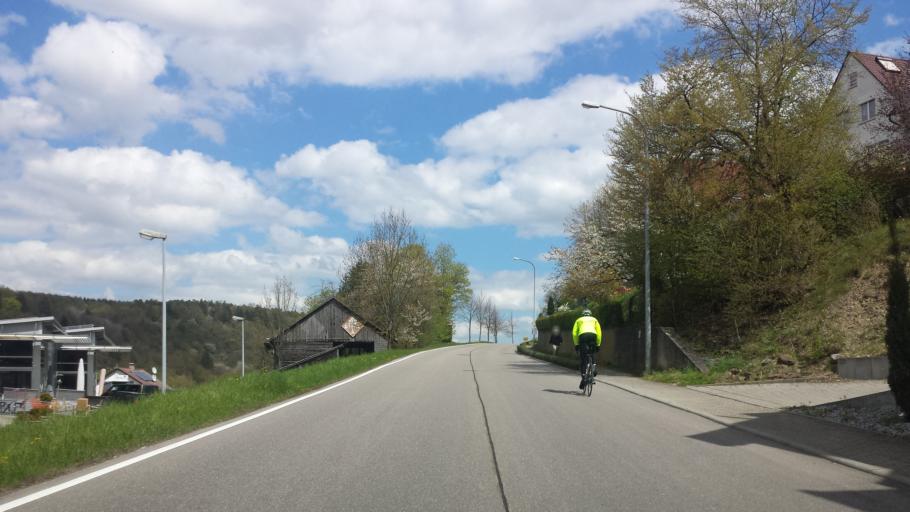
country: DE
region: Baden-Wuerttemberg
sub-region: Karlsruhe Region
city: Monsheim
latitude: 48.8660
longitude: 8.8676
